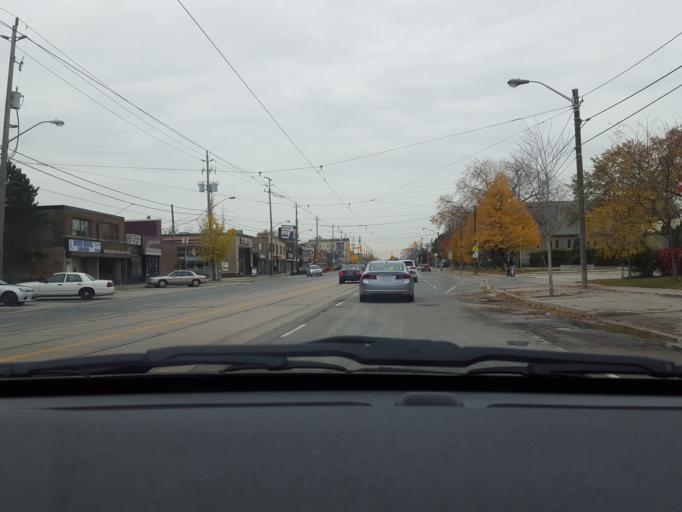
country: CA
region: Ontario
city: Etobicoke
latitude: 43.5939
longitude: -79.5360
